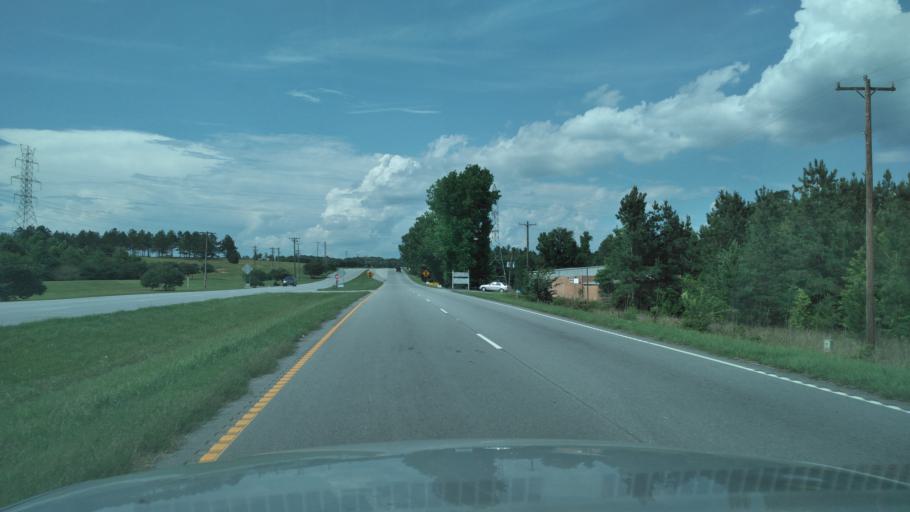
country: US
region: South Carolina
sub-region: Spartanburg County
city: Roebuck
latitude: 34.8487
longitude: -81.9673
